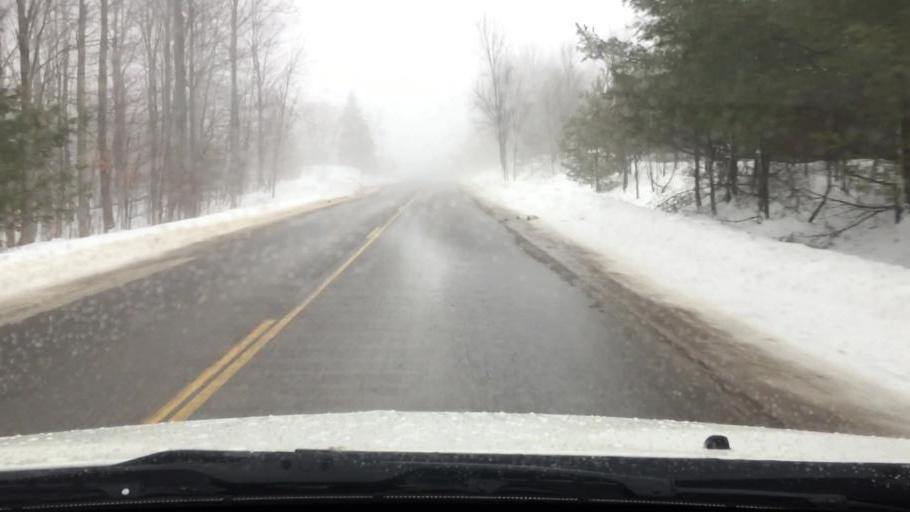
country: US
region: Michigan
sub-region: Charlevoix County
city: East Jordan
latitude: 45.1260
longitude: -85.1802
